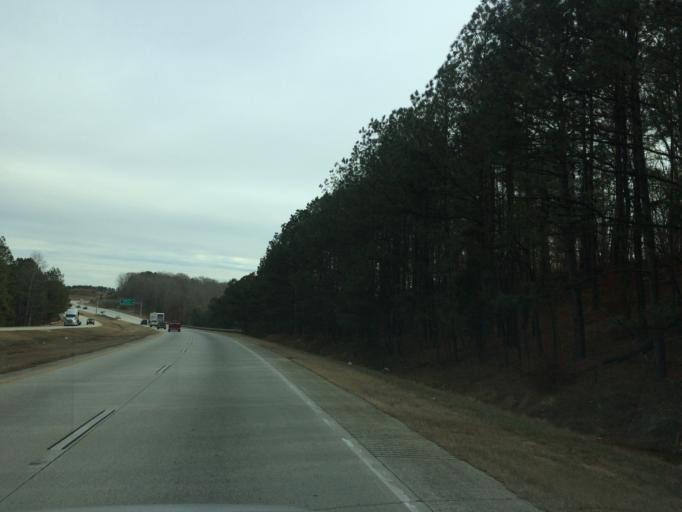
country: US
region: Georgia
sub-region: Gwinnett County
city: Dacula
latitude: 33.9751
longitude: -83.9179
